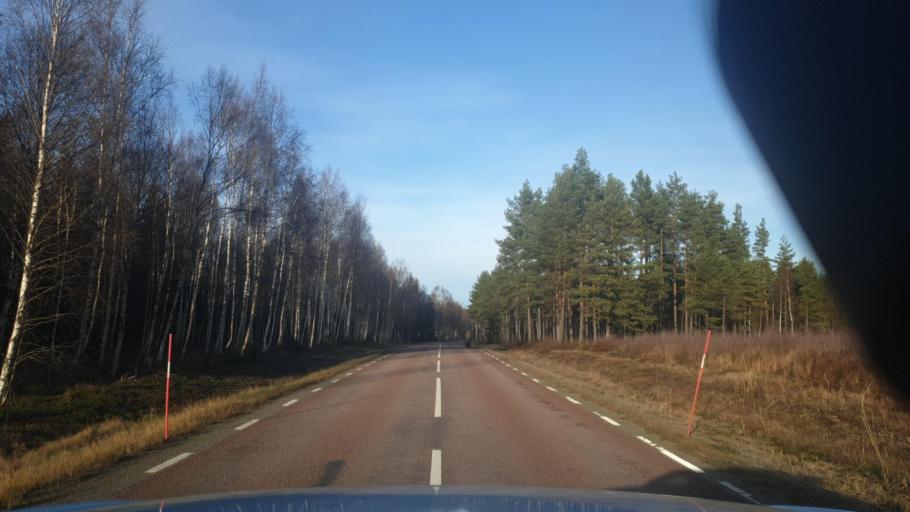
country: SE
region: Vaermland
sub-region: Grums Kommun
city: Grums
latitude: 59.4368
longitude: 12.9793
